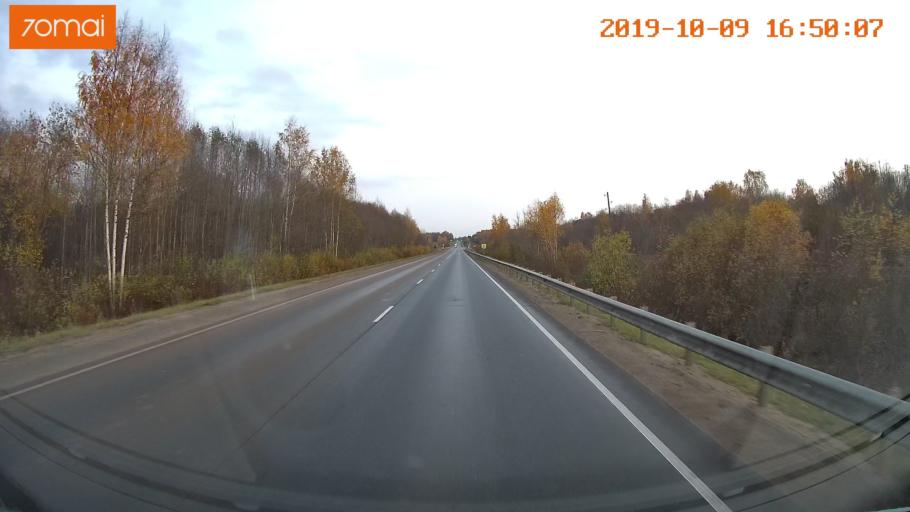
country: RU
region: Kostroma
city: Volgorechensk
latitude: 57.4053
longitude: 41.2048
